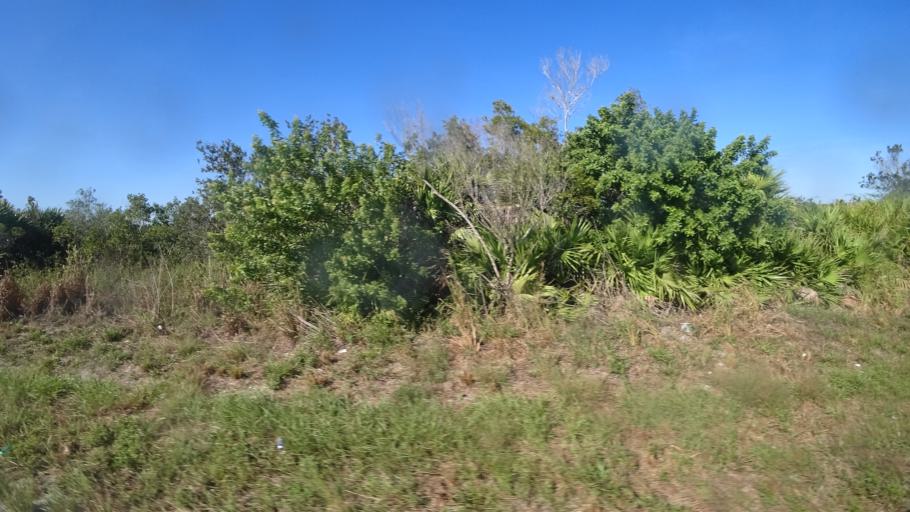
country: US
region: Florida
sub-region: Hillsborough County
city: Wimauma
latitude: 27.6074
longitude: -82.2927
